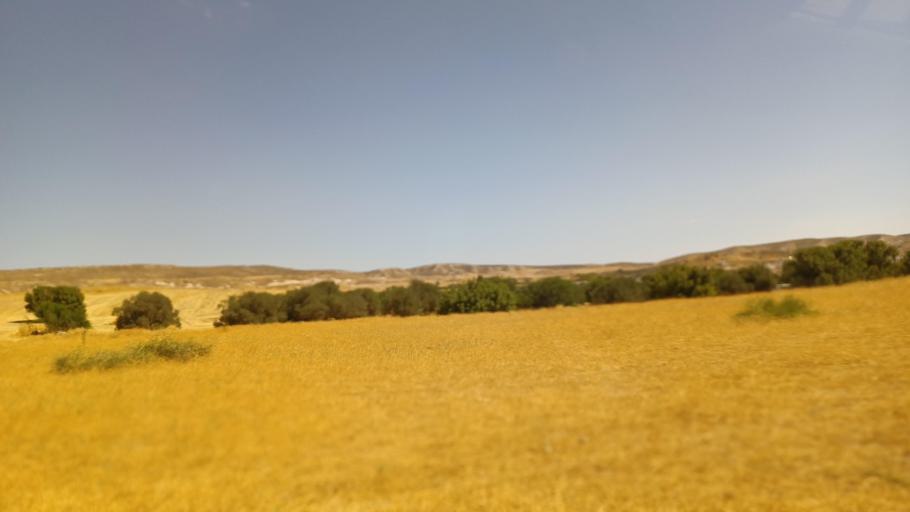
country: CY
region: Larnaka
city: Troulloi
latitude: 35.0235
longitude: 33.6016
